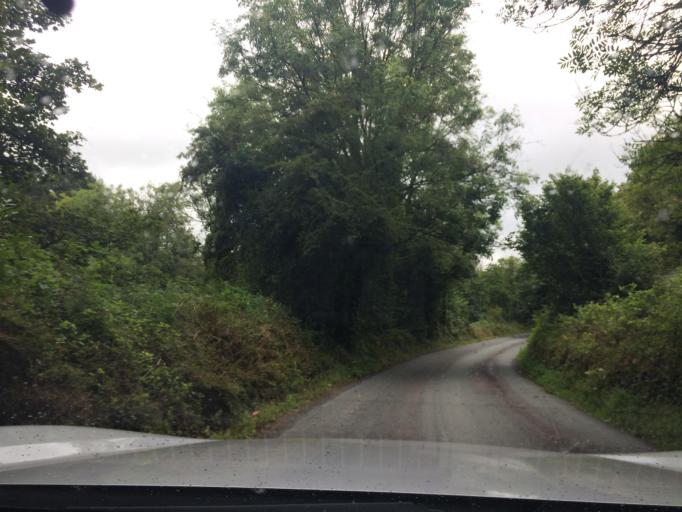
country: IE
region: Munster
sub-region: South Tipperary
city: Cluain Meala
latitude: 52.2086
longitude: -7.7320
